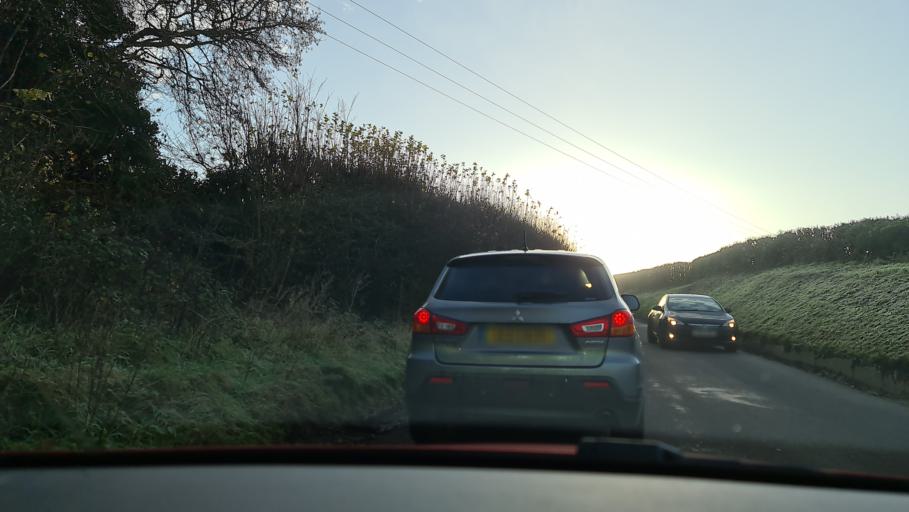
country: GB
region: England
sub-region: Buckinghamshire
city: Haddenham
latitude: 51.8076
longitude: -0.9558
